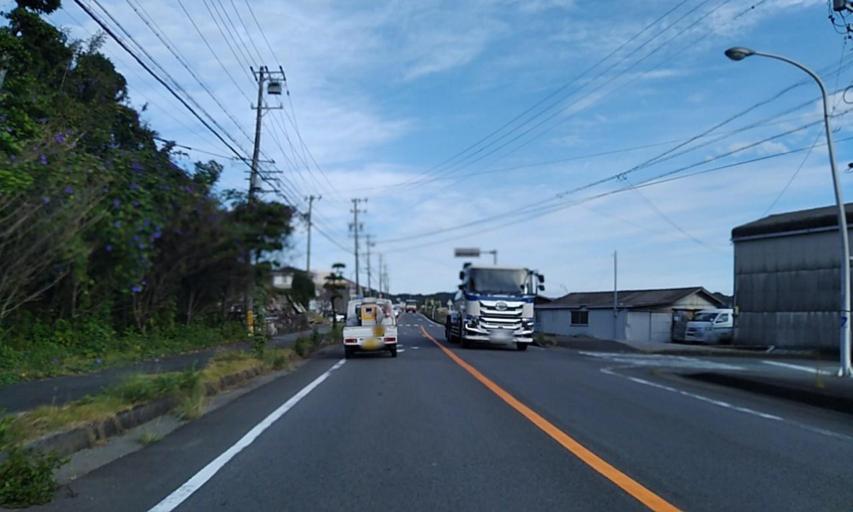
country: JP
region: Mie
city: Ise
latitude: 34.3486
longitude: 136.6931
